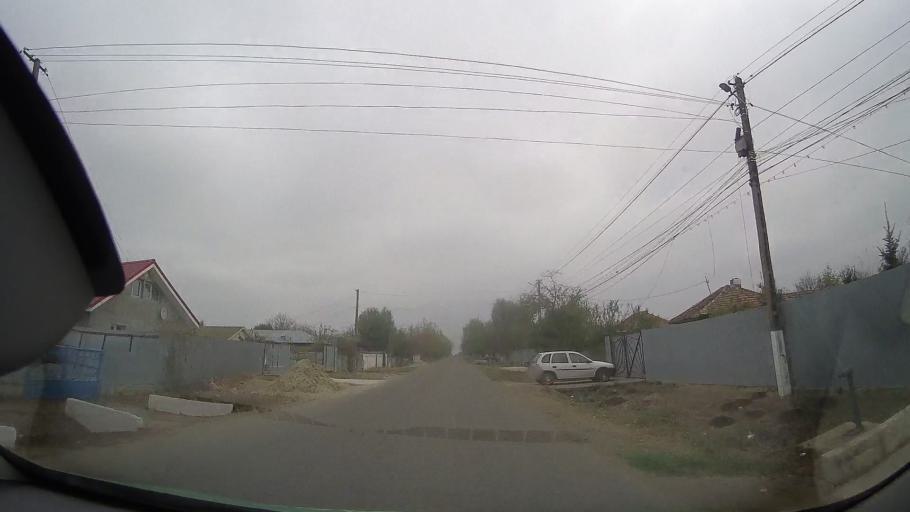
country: RO
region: Buzau
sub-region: Comuna Glodeanu-Silistea
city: Glodeanu-Silistea
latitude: 44.8197
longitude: 26.8367
